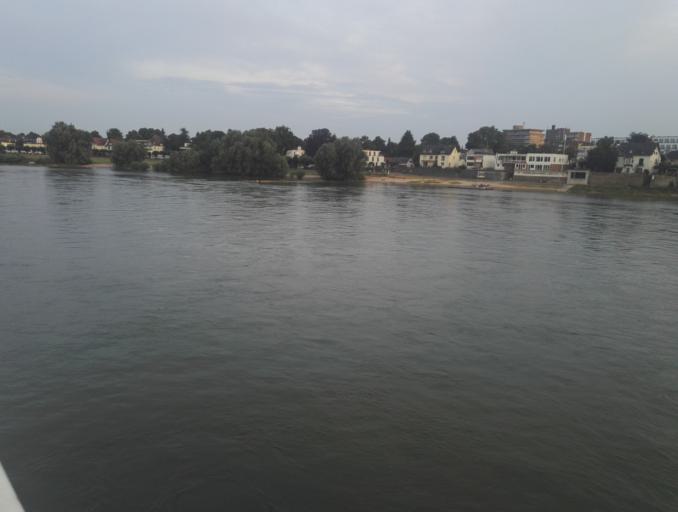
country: DE
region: North Rhine-Westphalia
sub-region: Regierungsbezirk Koln
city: Poll
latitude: 50.8963
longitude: 6.9986
